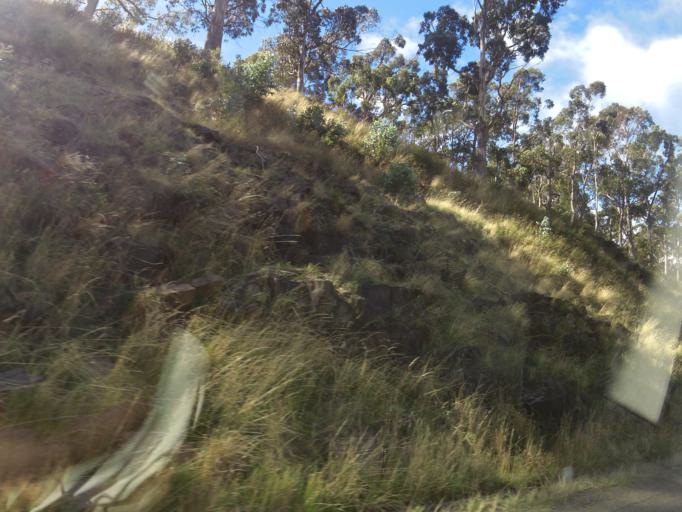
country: AU
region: Tasmania
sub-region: Kingborough
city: Kingston
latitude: -42.9661
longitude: 147.2529
